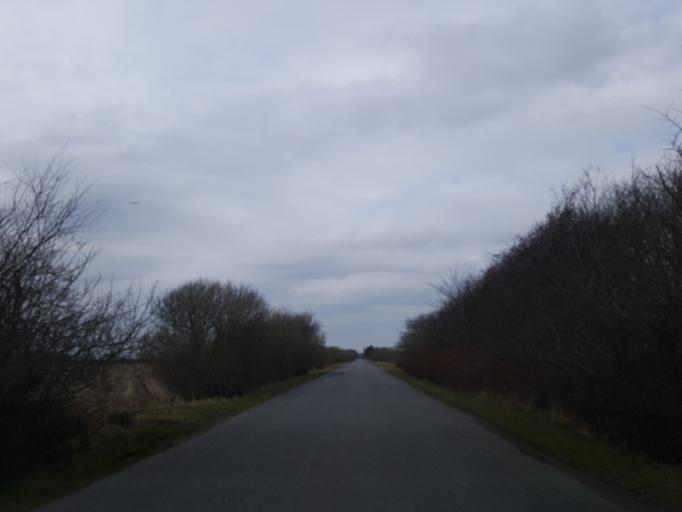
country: DK
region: Central Jutland
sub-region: Holstebro Kommune
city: Ulfborg
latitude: 56.3529
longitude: 8.2781
